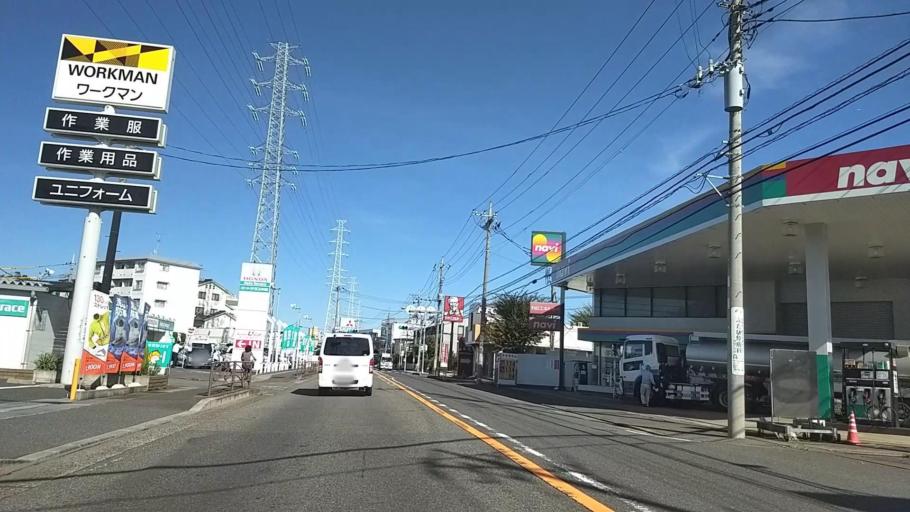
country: JP
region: Kanagawa
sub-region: Kawasaki-shi
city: Kawasaki
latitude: 35.5682
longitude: 139.6369
